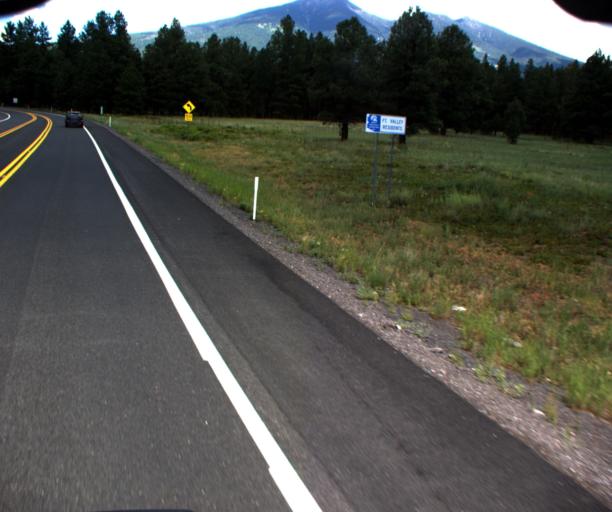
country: US
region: Arizona
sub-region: Coconino County
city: Flagstaff
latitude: 35.2646
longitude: -111.7051
